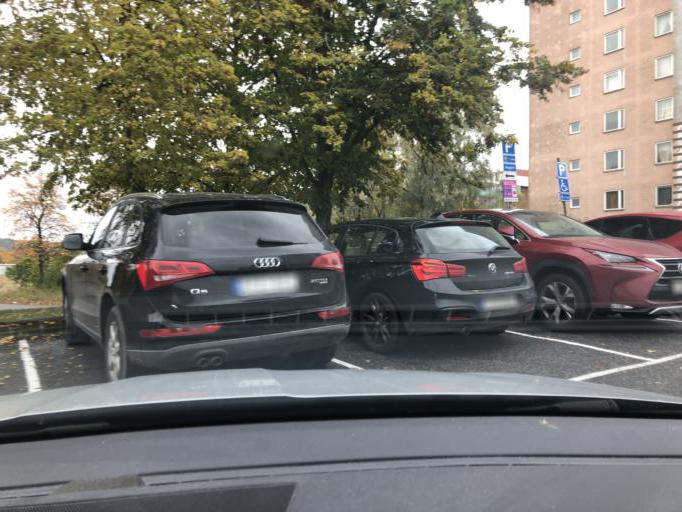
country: SE
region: Stockholm
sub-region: Botkyrka Kommun
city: Alby
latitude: 59.2380
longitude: 17.8471
